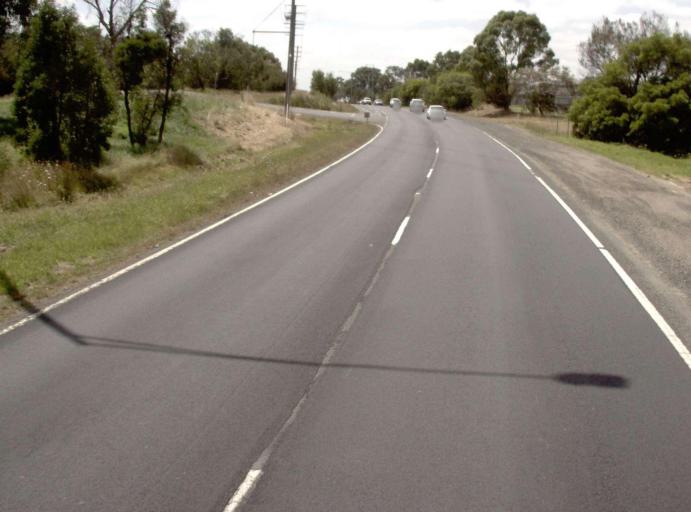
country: AU
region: Victoria
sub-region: Cardinia
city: Officer
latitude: -38.0650
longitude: 145.4269
